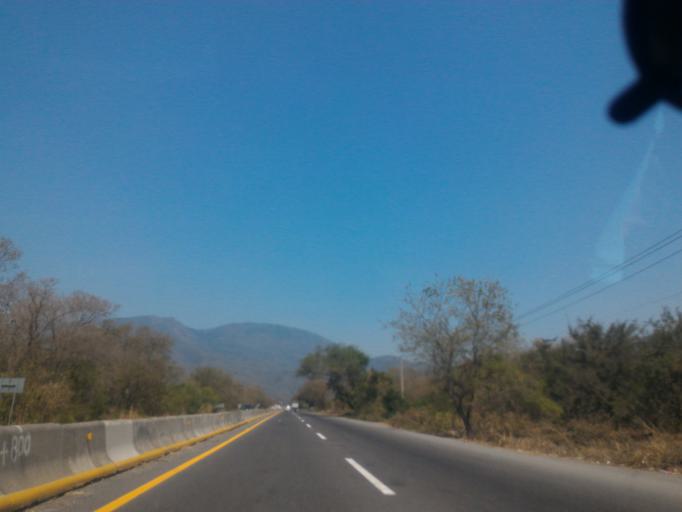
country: MX
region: Colima
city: Tecoman
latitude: 18.9964
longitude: -103.8391
